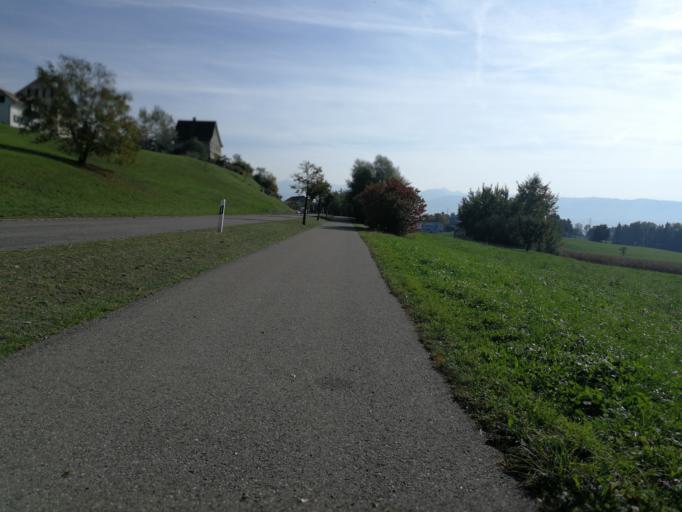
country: CH
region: Zurich
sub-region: Bezirk Hinwil
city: Hadlikon
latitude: 47.2928
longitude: 8.8525
